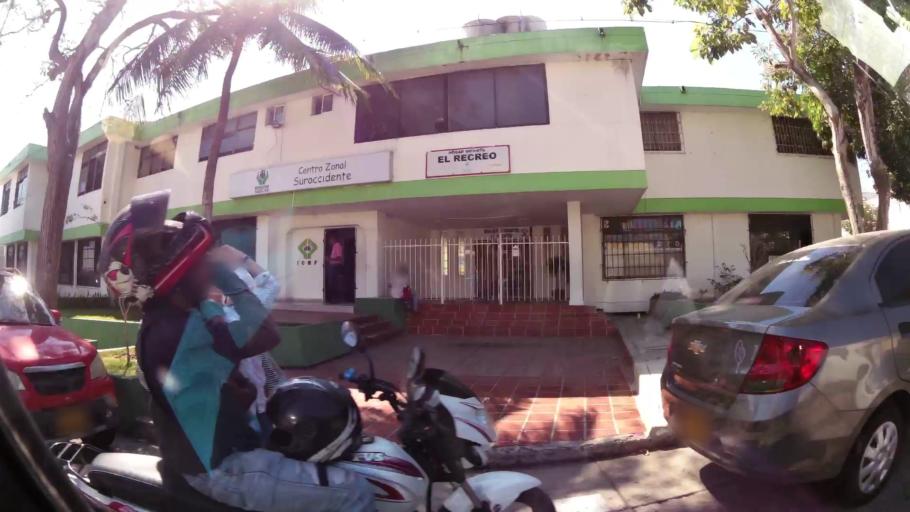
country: CO
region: Atlantico
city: Barranquilla
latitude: 10.9845
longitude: -74.8033
